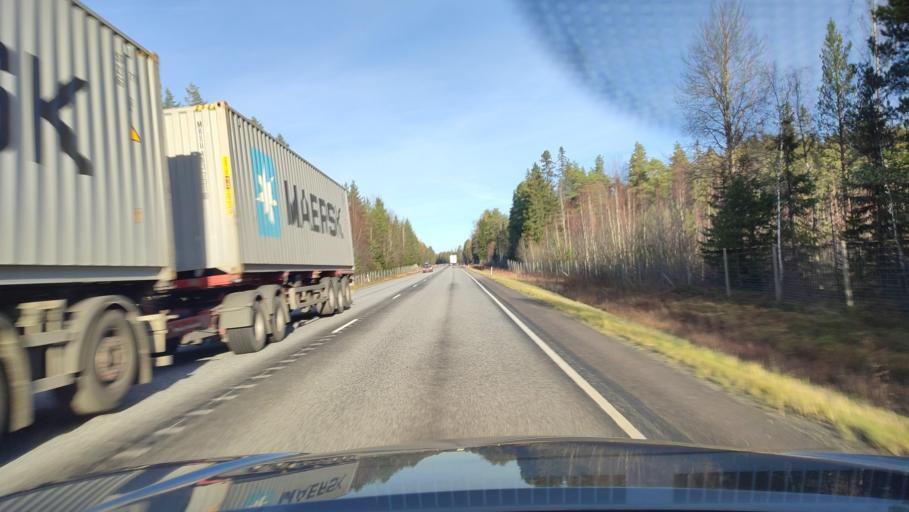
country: FI
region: Ostrobothnia
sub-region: Vaasa
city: Malax
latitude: 62.8311
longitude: 21.6932
